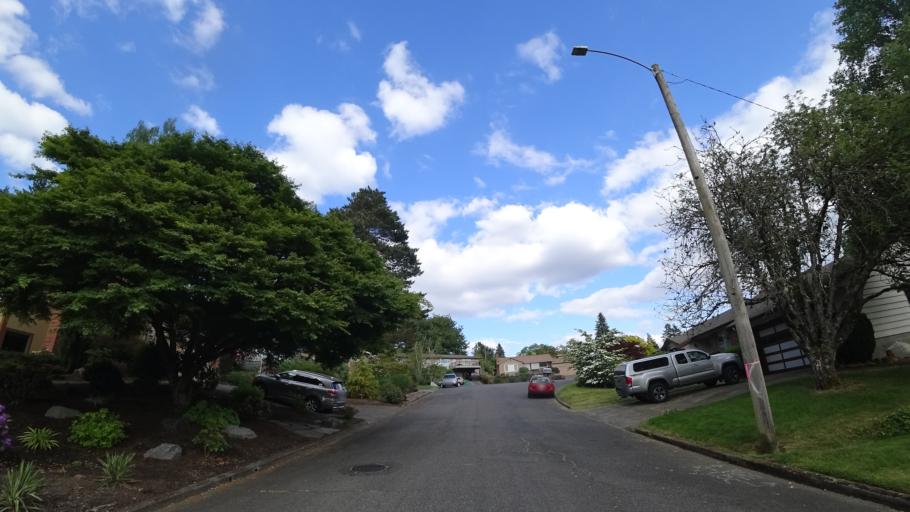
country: US
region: Oregon
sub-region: Washington County
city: Garden Home-Whitford
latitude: 45.4771
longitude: -122.7168
